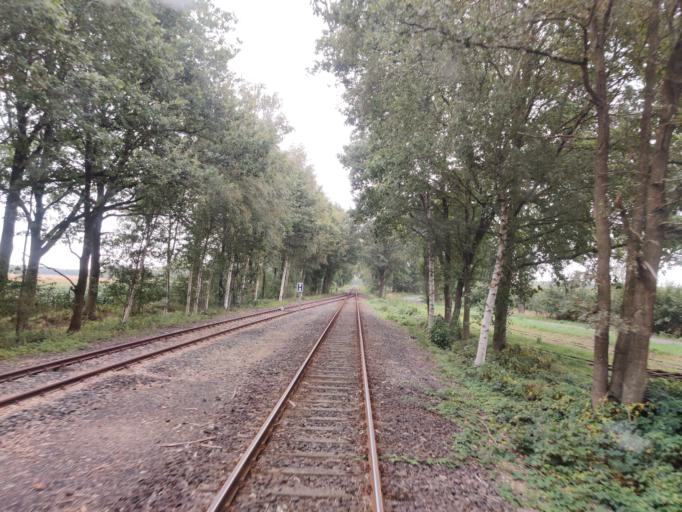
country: DE
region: Lower Saxony
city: Deinste
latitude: 53.5349
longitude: 9.4459
